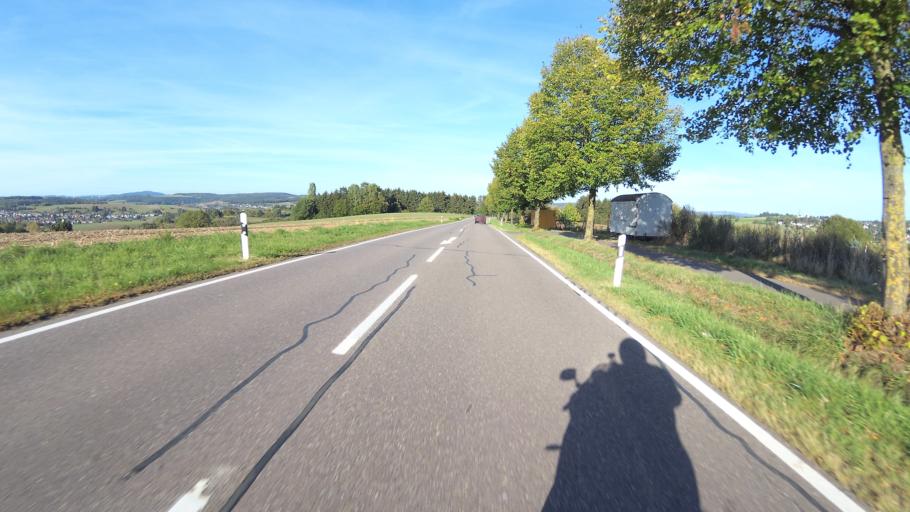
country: DE
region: Saarland
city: Illingen
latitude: 49.3632
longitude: 7.0319
